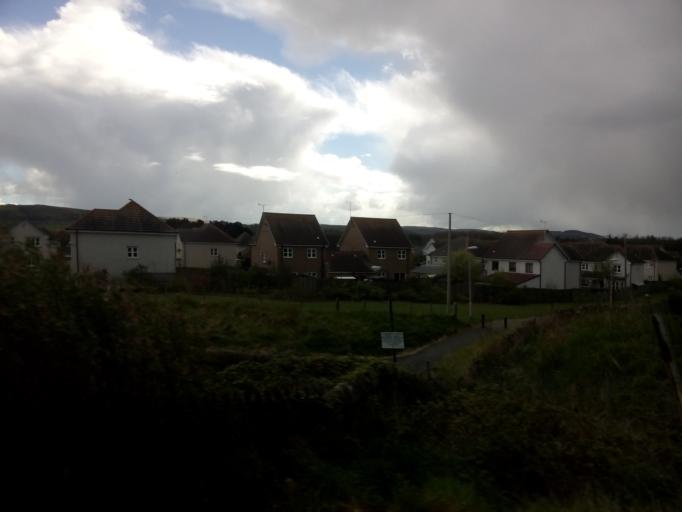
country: GB
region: Scotland
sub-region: East Lothian
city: Dunbar
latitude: 55.9988
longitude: -2.5162
